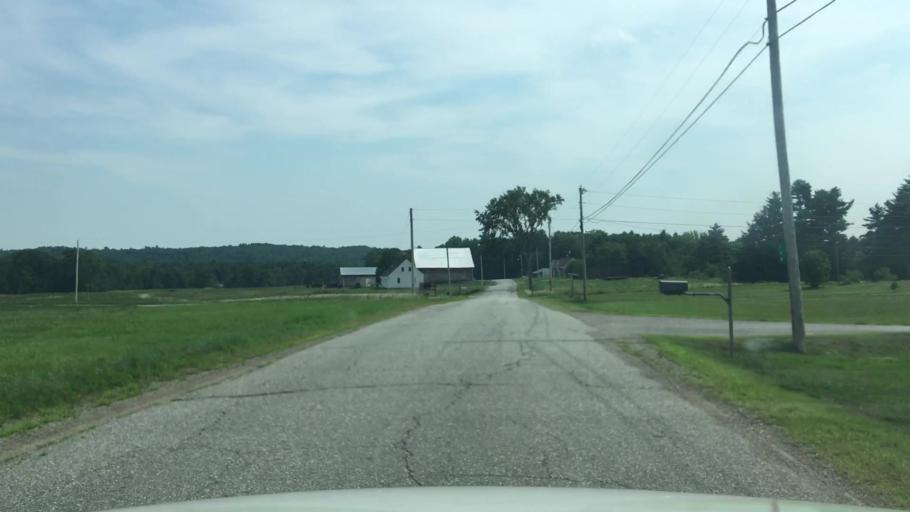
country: US
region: Maine
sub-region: Lincoln County
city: Jefferson
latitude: 44.2207
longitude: -69.4482
